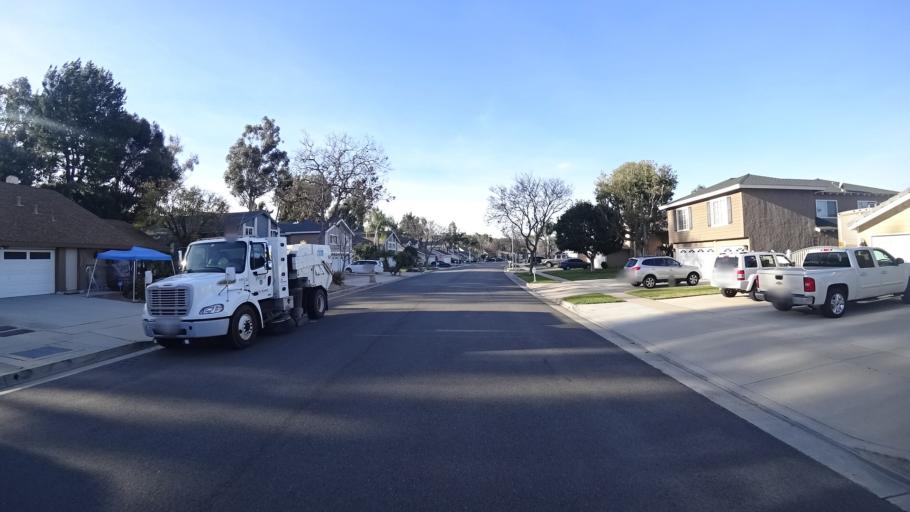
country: US
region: California
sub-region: Orange County
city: Yorba Linda
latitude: 33.8630
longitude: -117.7654
